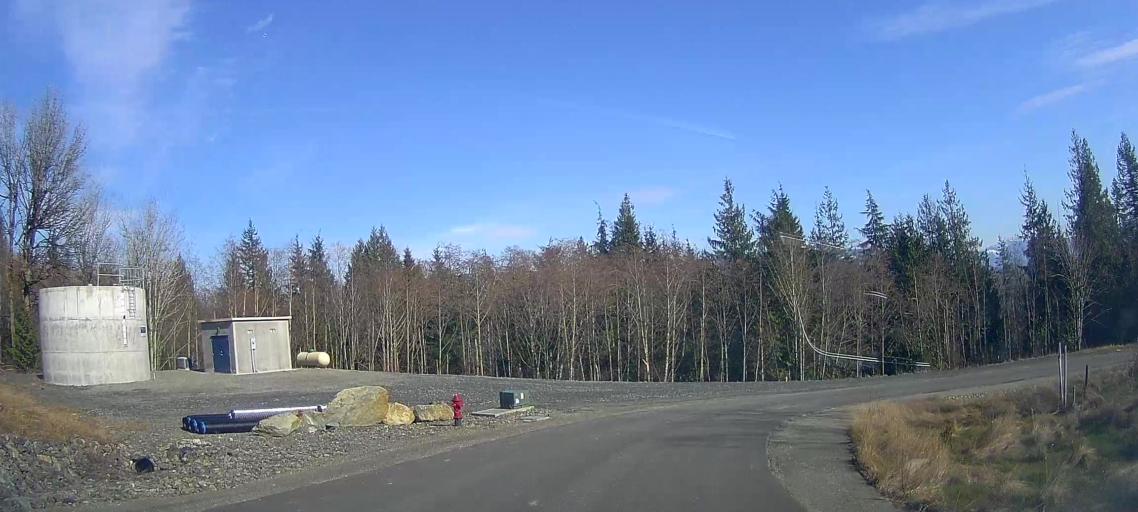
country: US
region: Washington
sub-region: Whatcom County
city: Sudden Valley
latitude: 48.5982
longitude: -122.3848
